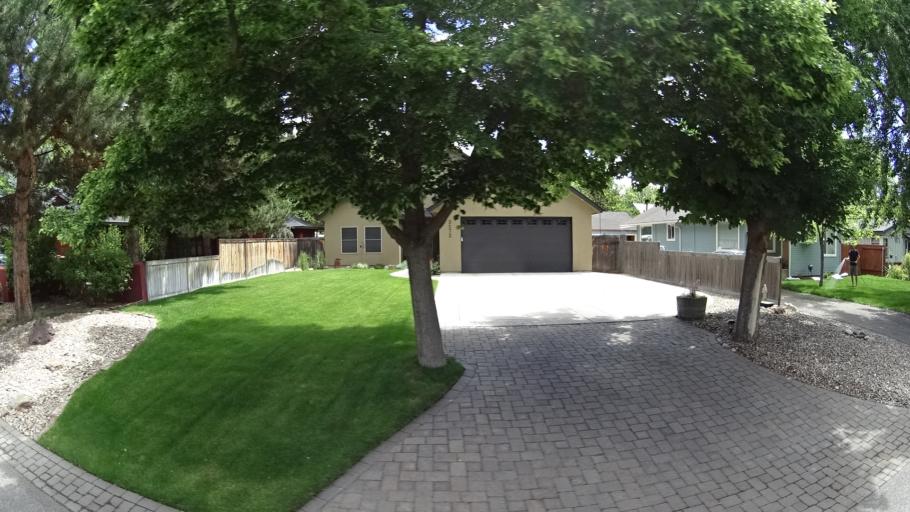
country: US
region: Idaho
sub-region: Ada County
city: Boise
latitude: 43.5845
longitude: -116.1987
